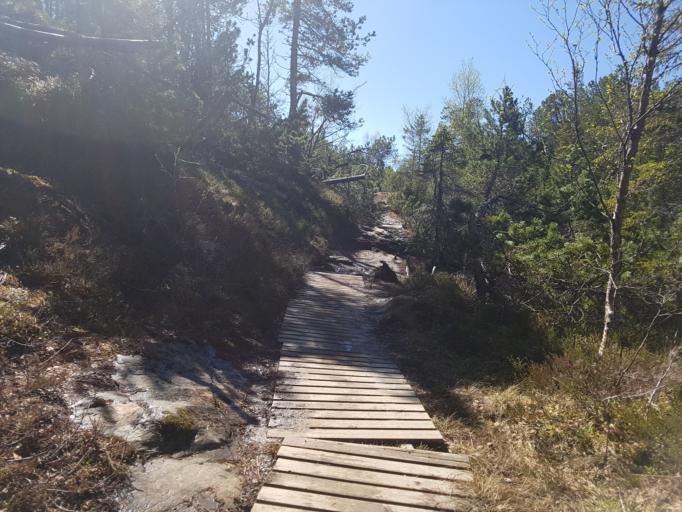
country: NO
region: Sor-Trondelag
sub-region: Trondheim
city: Trondheim
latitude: 63.4338
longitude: 10.3143
